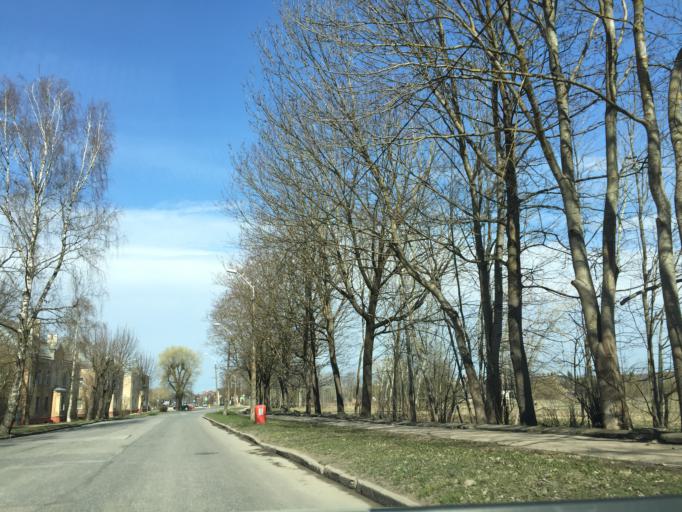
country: EE
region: Ida-Virumaa
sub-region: Narva linn
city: Narva
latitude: 59.3847
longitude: 28.1993
